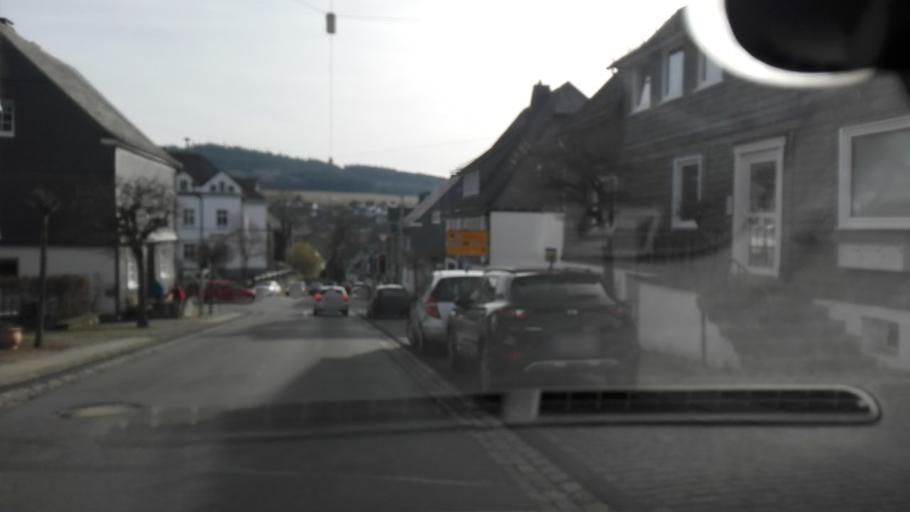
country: DE
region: North Rhine-Westphalia
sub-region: Regierungsbezirk Arnsberg
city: Schmallenberg
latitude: 51.1467
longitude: 8.2847
